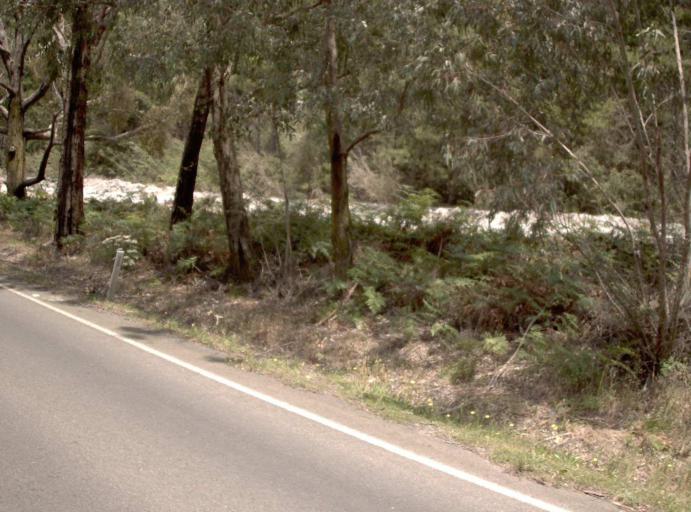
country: AU
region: Victoria
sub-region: Latrobe
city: Traralgon
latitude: -38.2682
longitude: 146.6916
